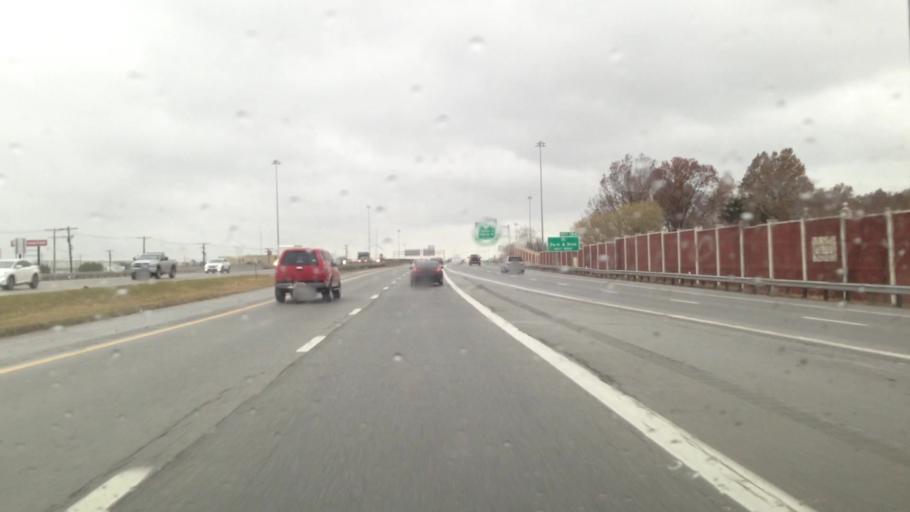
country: US
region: Ohio
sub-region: Cuyahoga County
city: Euclid
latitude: 41.6035
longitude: -81.4996
